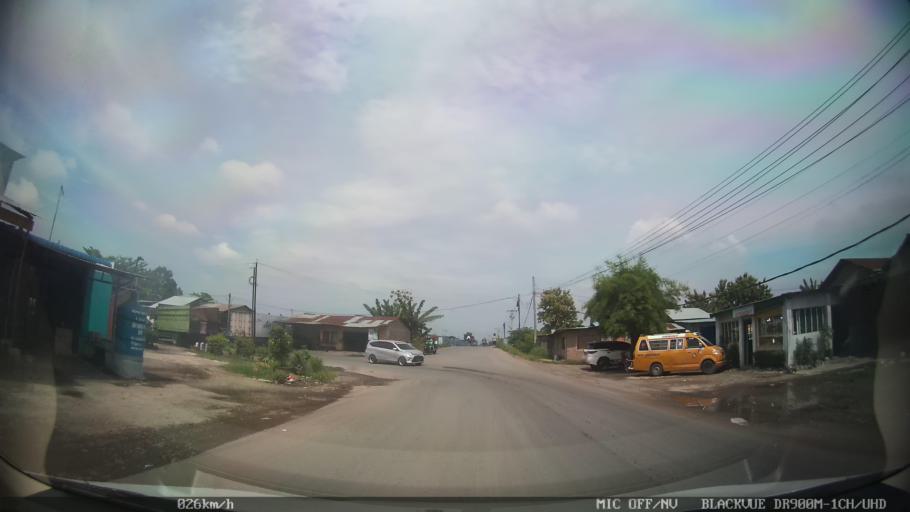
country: ID
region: North Sumatra
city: Medan
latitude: 3.6507
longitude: 98.7097
